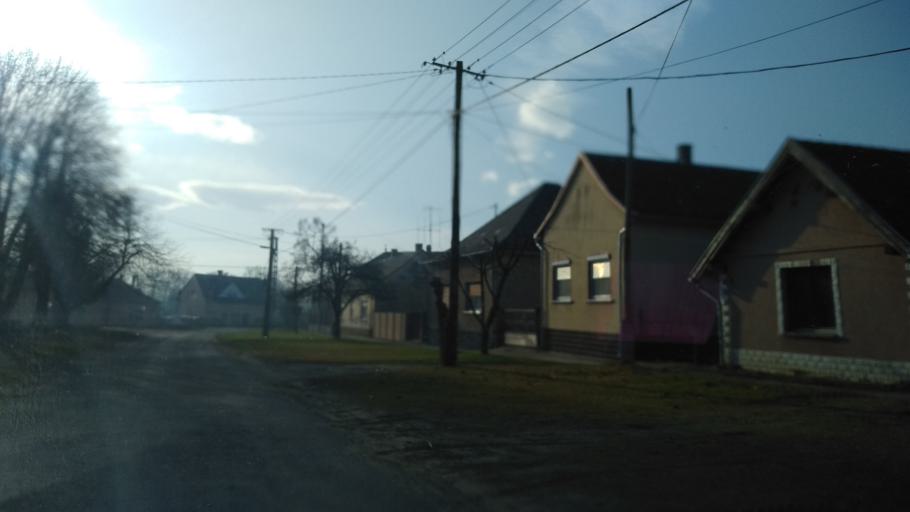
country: HU
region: Somogy
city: Barcs
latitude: 45.9623
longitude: 17.4780
